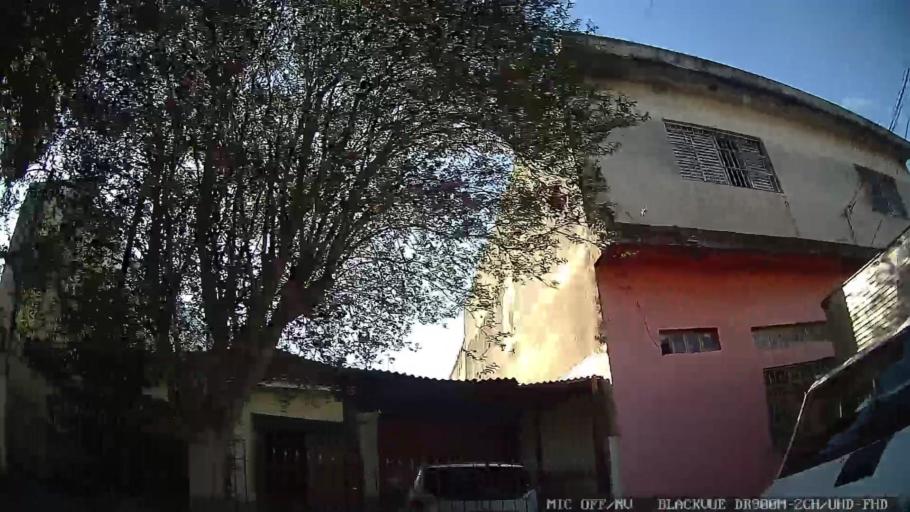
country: BR
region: Sao Paulo
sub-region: Guarulhos
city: Guarulhos
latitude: -23.5314
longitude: -46.5067
